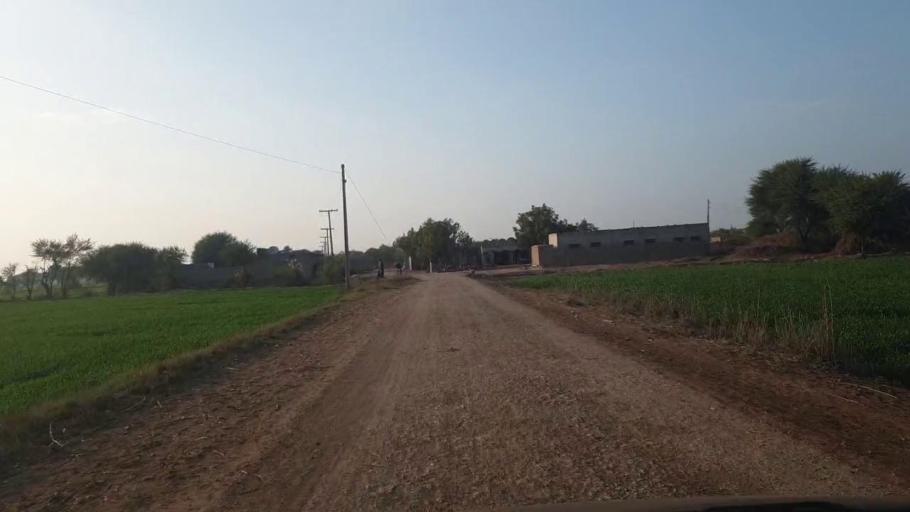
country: PK
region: Sindh
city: Berani
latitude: 25.8608
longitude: 68.7353
